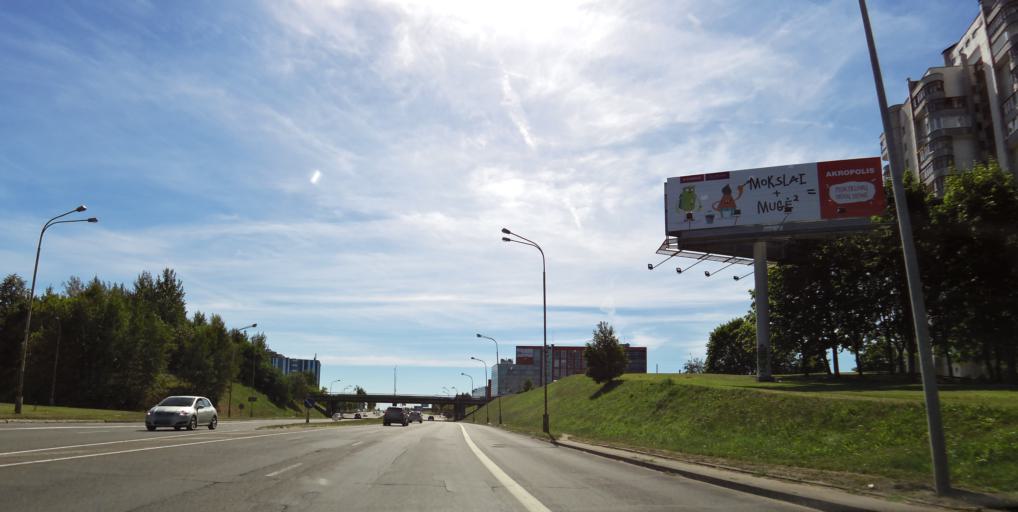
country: LT
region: Vilnius County
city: Seskine
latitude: 54.7183
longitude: 25.2458
